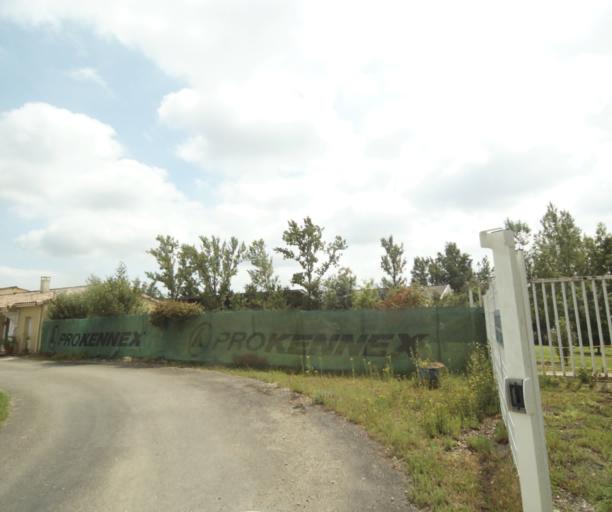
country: FR
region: Midi-Pyrenees
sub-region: Departement du Tarn-et-Garonne
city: Albias
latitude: 44.0588
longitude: 1.4051
